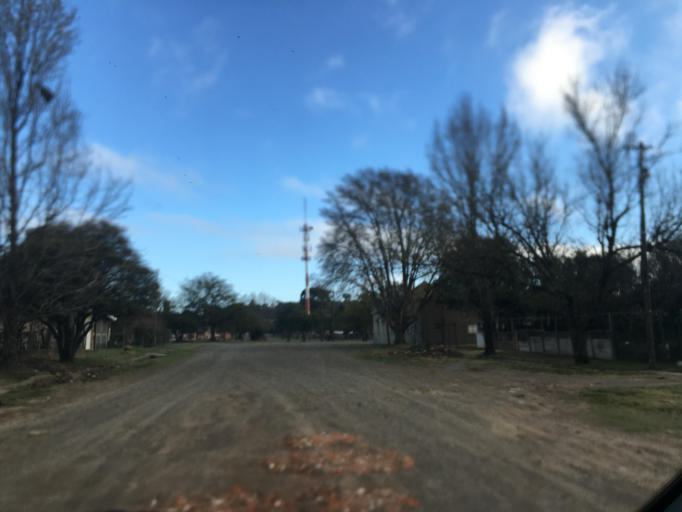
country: ZA
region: Eastern Cape
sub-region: Chris Hani District Municipality
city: Elliot
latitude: -31.3356
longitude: 27.8510
